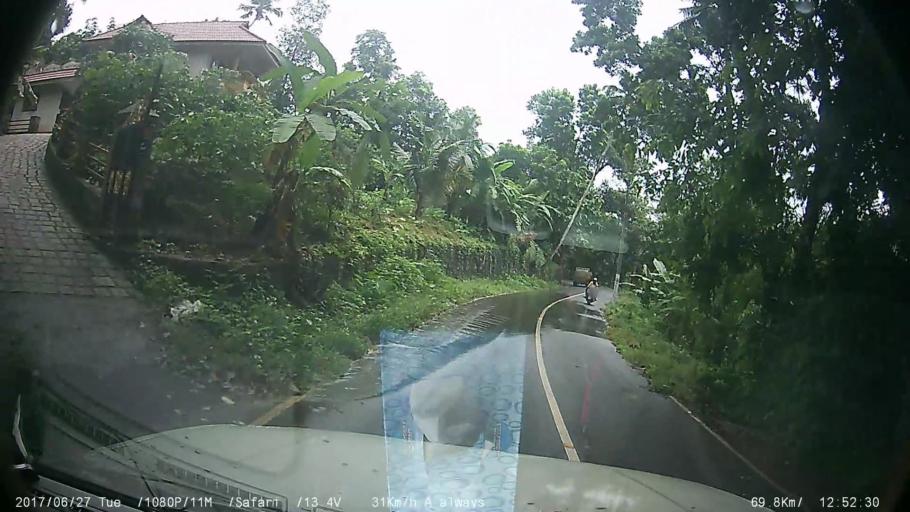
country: IN
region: Kerala
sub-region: Ernakulam
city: Piravam
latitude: 9.7830
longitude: 76.5416
